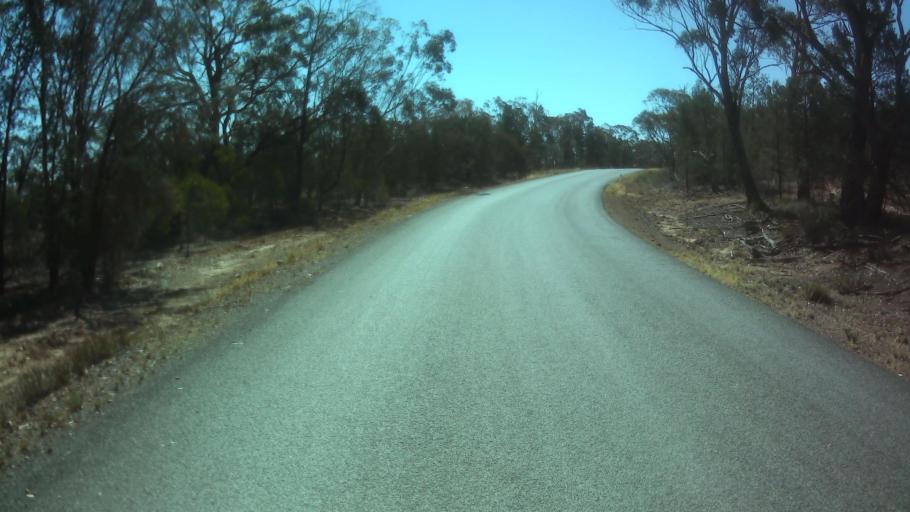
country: AU
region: New South Wales
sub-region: Weddin
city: Grenfell
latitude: -33.8057
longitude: 147.8985
